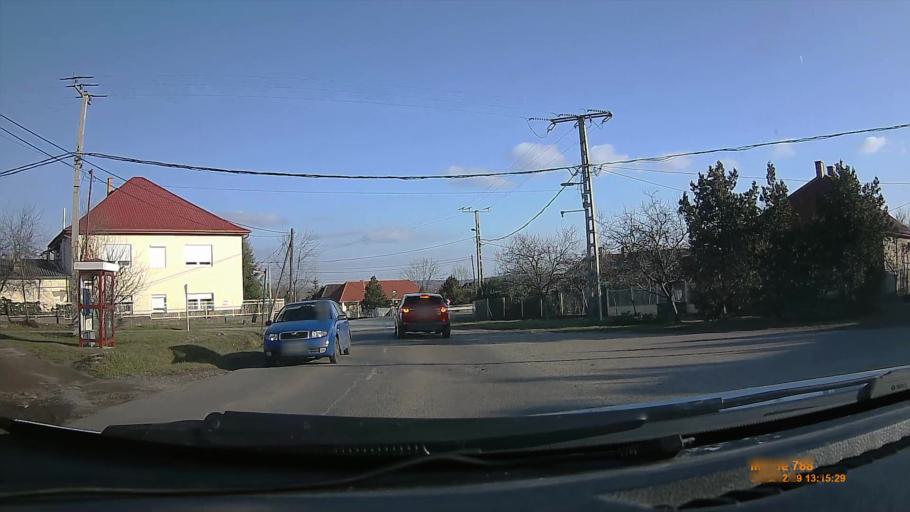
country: HU
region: Heves
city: Domoszlo
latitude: 47.8276
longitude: 20.1105
